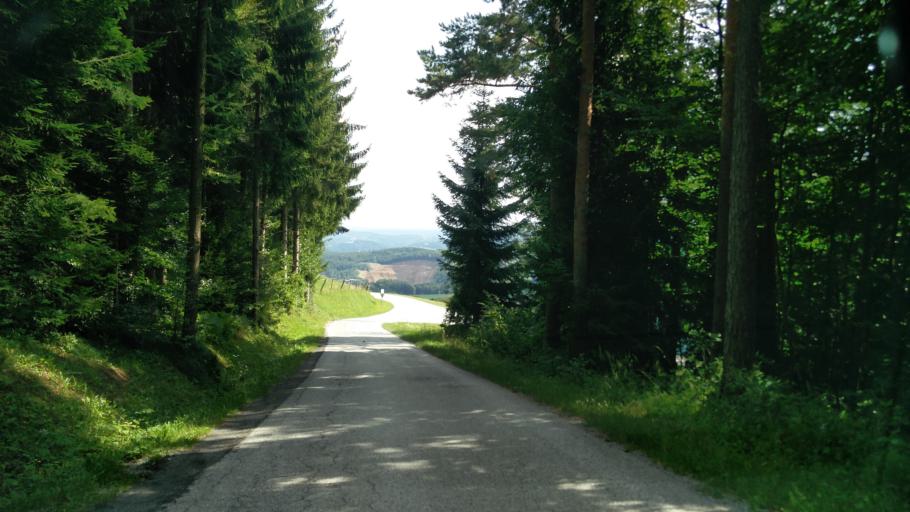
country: AT
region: Styria
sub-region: Politischer Bezirk Weiz
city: Naas
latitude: 47.2557
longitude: 15.6043
